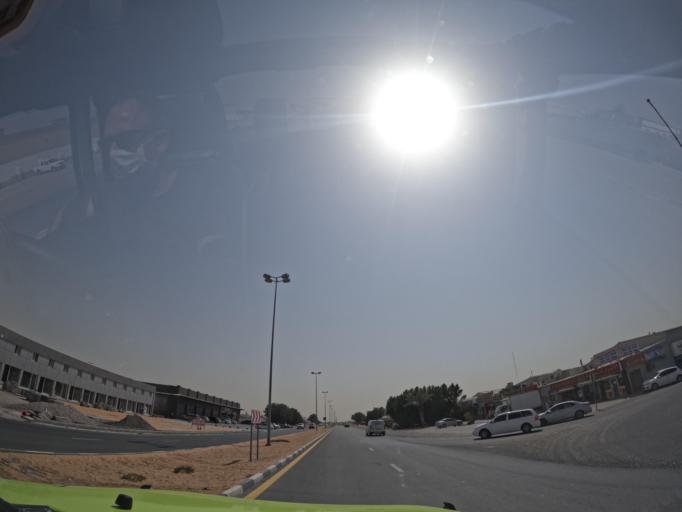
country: AE
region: Umm al Qaywayn
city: Umm al Qaywayn
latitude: 25.5036
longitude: 55.5610
